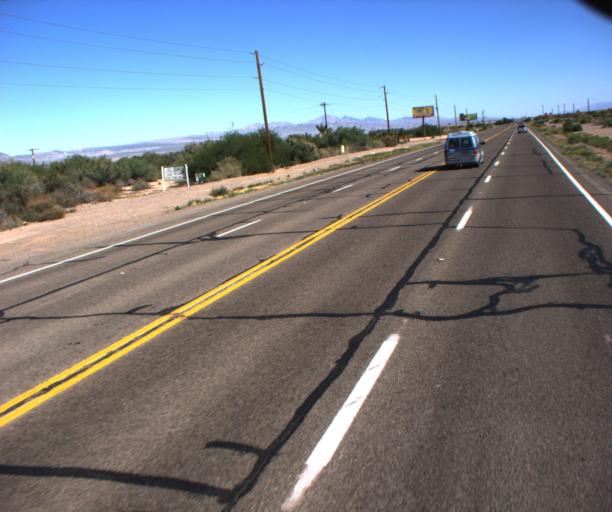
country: US
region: Arizona
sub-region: Mohave County
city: Mohave Valley
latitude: 34.9486
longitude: -114.5979
